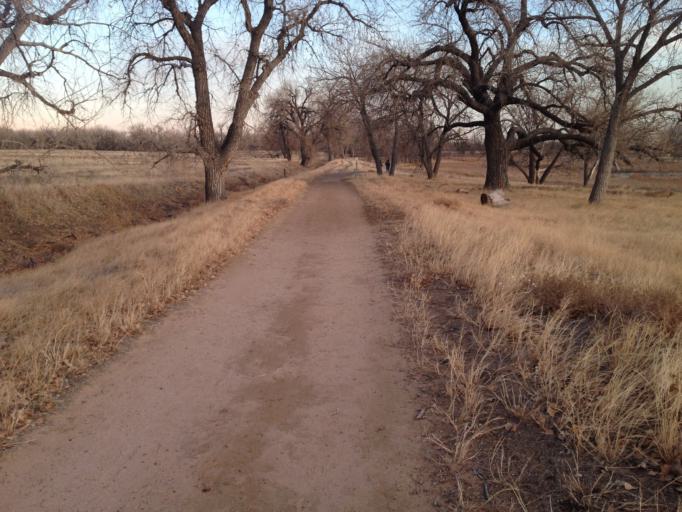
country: US
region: Colorado
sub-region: Adams County
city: Derby
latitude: 39.8152
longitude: -104.8540
